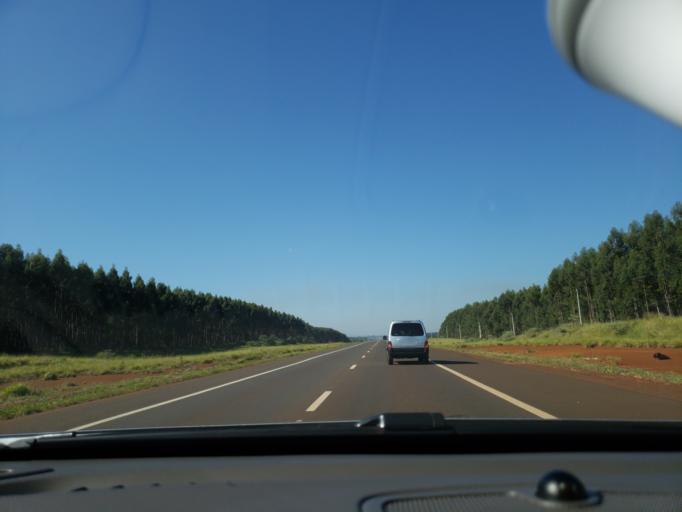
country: AR
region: Misiones
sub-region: Departamento de Capital
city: Posadas
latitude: -27.4653
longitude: -55.9496
